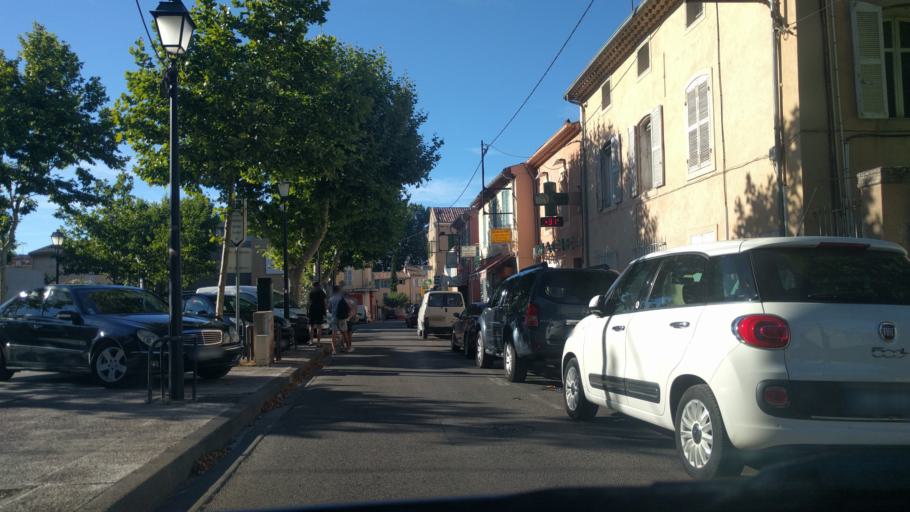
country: FR
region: Provence-Alpes-Cote d'Azur
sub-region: Departement des Bouches-du-Rhone
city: Bouc-Bel-Air
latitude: 43.5037
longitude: 5.3876
